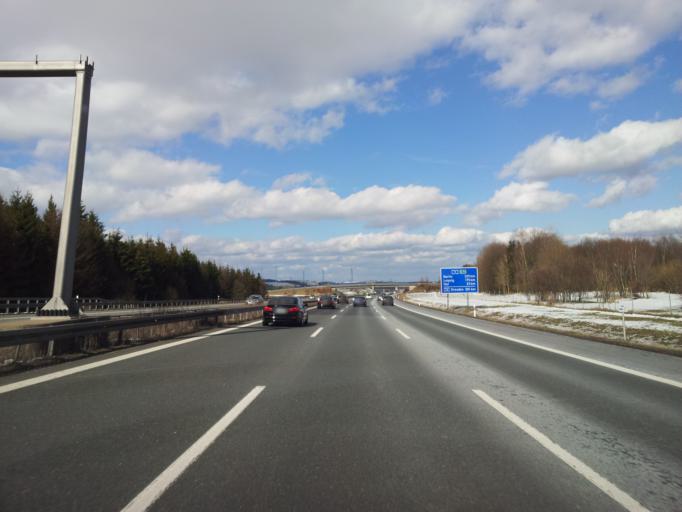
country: DE
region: Bavaria
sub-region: Upper Franconia
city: Munchberg
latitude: 50.1745
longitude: 11.7491
